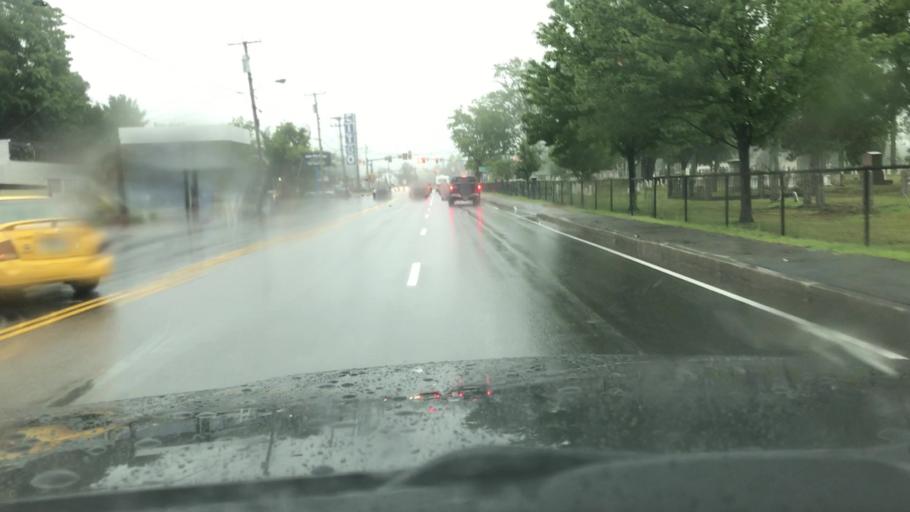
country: US
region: Maine
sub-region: York County
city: Biddeford
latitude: 43.4815
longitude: -70.4727
